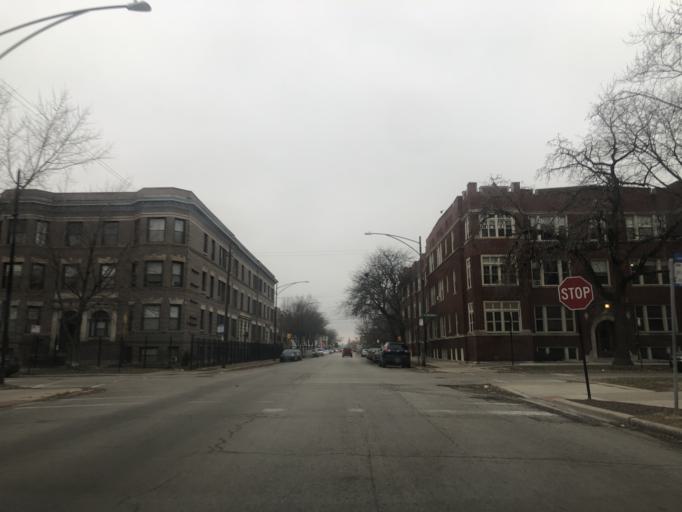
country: US
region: Illinois
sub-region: Cook County
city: Chicago
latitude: 41.7841
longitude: -87.6024
